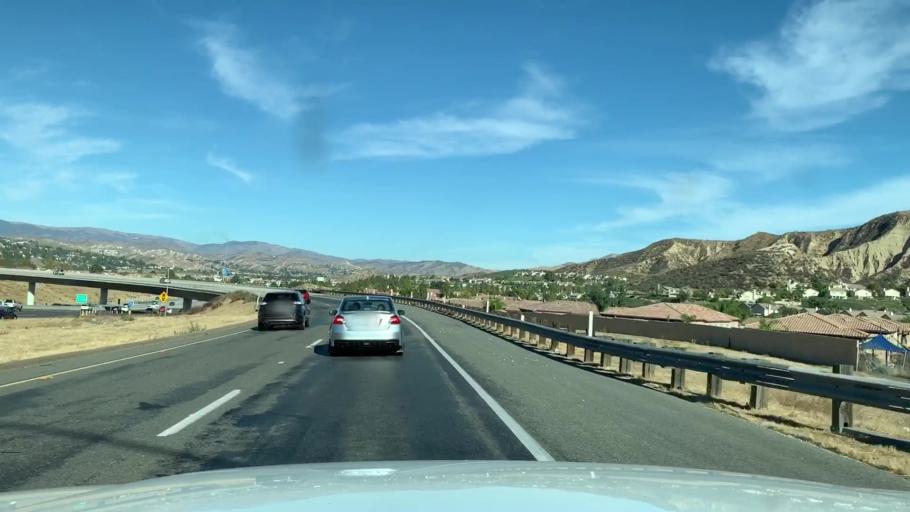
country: US
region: California
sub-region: Los Angeles County
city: Santa Clarita
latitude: 34.4003
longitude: -118.4580
